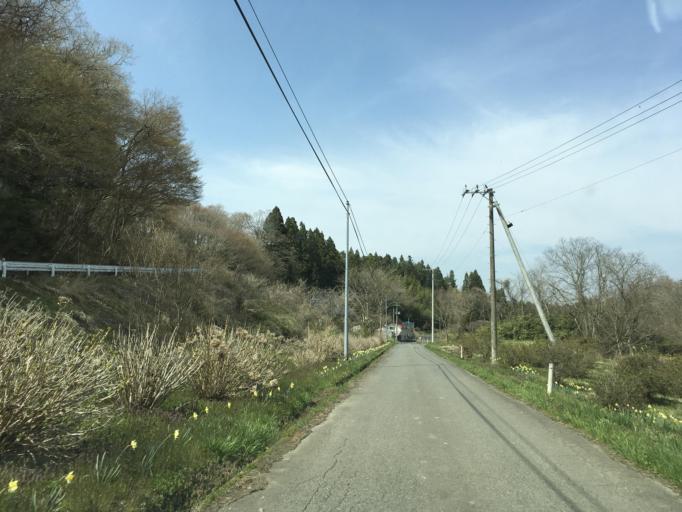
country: JP
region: Iwate
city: Ichinoseki
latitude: 38.8306
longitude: 141.3513
